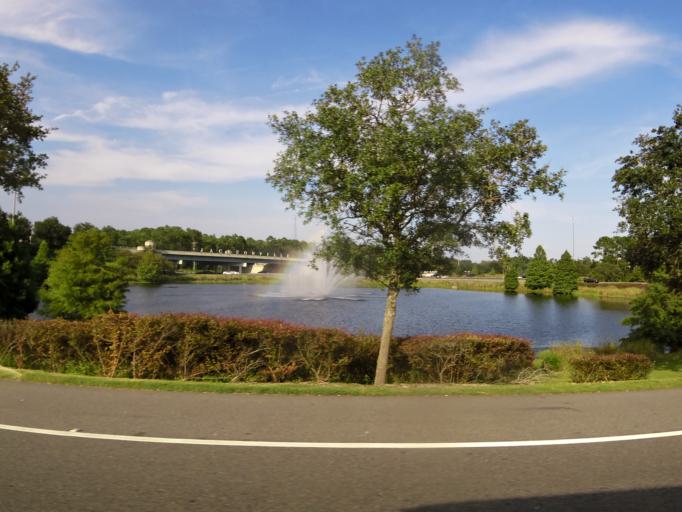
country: US
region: Florida
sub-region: Saint Johns County
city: Fruit Cove
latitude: 30.1399
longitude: -81.5422
